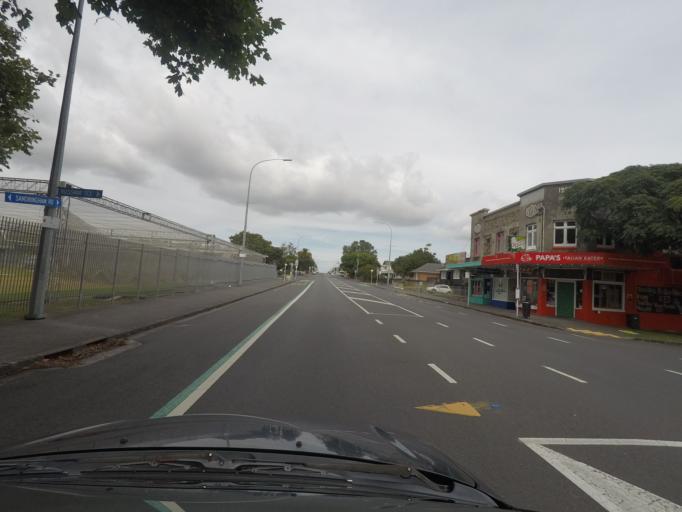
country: NZ
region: Auckland
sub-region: Auckland
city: Auckland
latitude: -36.8746
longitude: 174.7419
